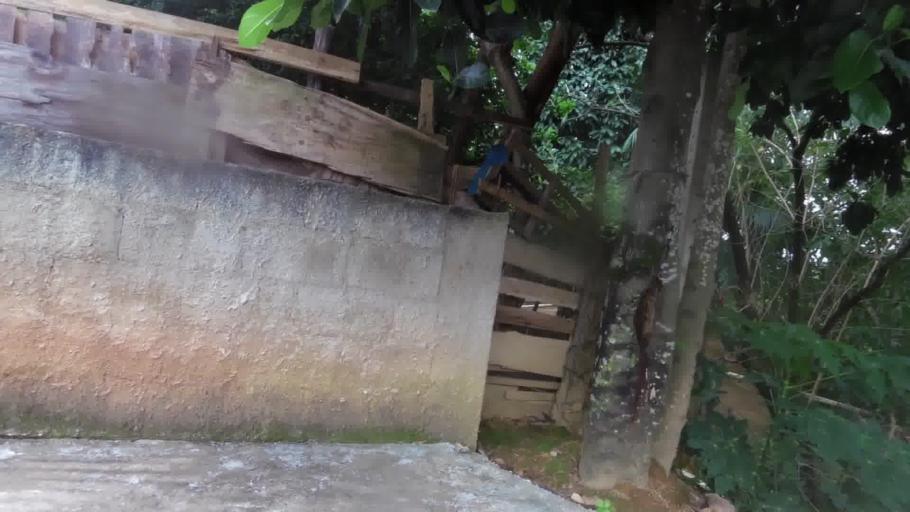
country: BR
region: Espirito Santo
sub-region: Alfredo Chaves
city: Alfredo Chaves
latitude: -20.6419
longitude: -40.7426
